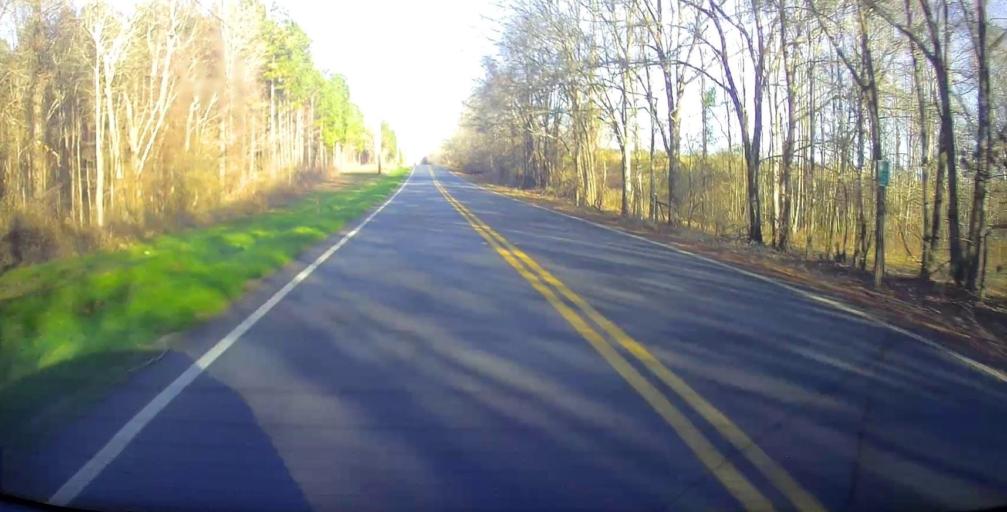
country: US
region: Georgia
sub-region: Harris County
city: Pine Mountain
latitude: 32.9162
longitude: -84.7904
